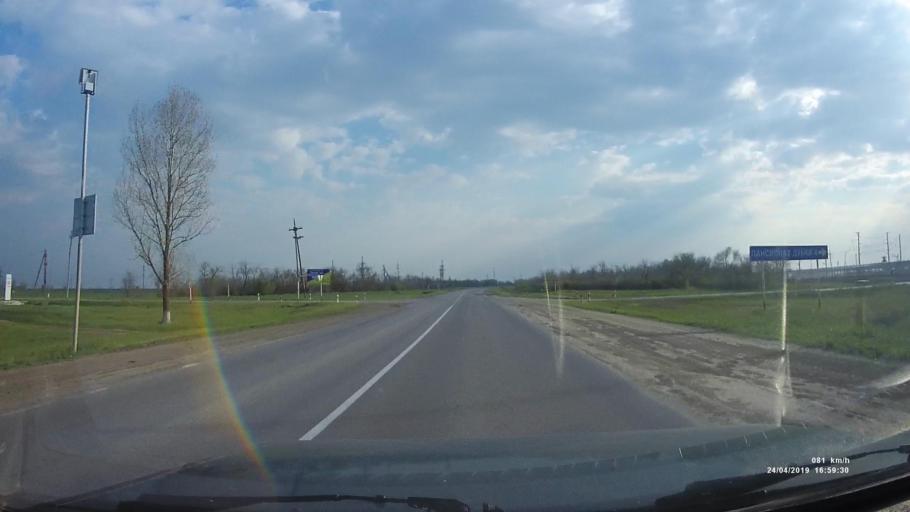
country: RU
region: Rostov
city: Proletarsk
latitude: 46.6173
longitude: 41.6502
